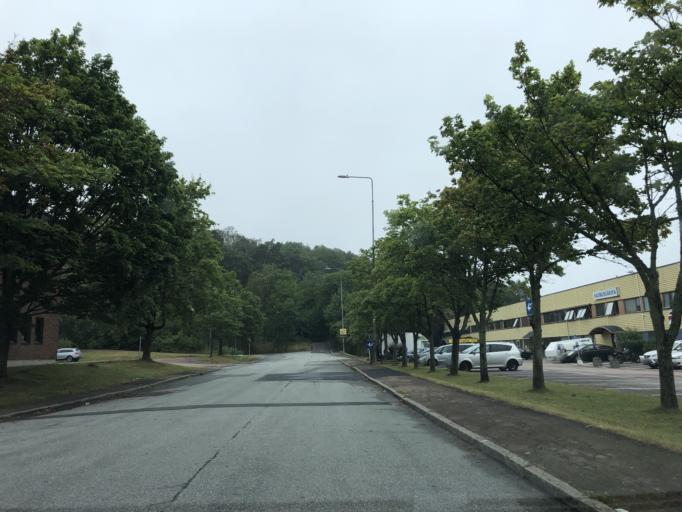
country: SE
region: Vaestra Goetaland
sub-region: Goteborg
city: Goeteborg
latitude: 57.7324
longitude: 11.9444
